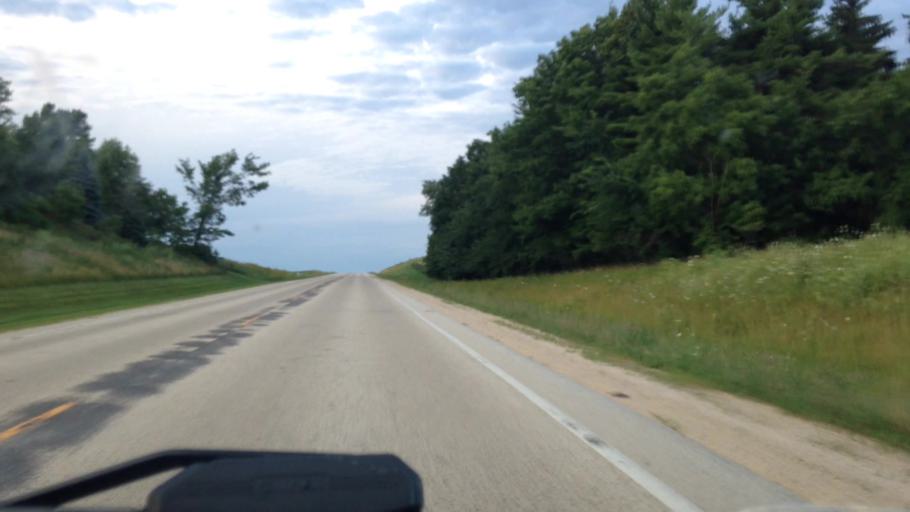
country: US
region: Wisconsin
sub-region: Dodge County
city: Theresa
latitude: 43.4629
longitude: -88.4502
